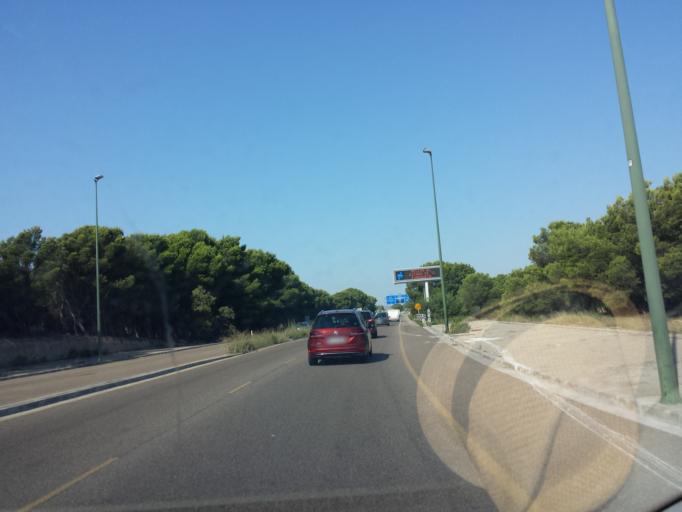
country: ES
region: Aragon
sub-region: Provincia de Zaragoza
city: Montecanal
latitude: 41.6376
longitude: -0.9614
